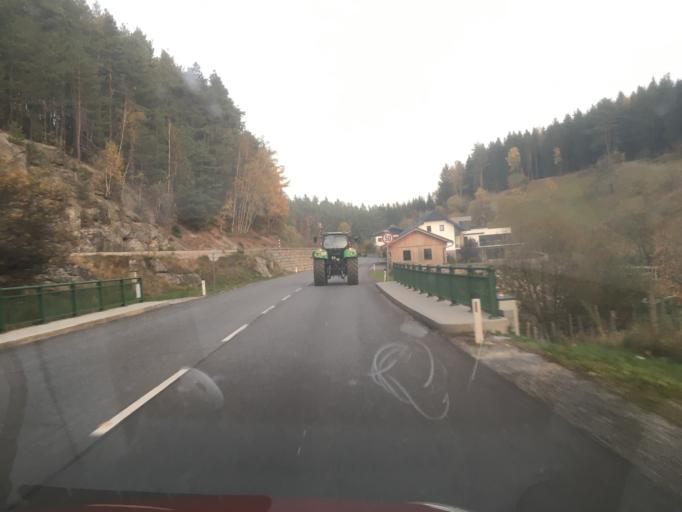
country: AT
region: Lower Austria
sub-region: Politischer Bezirk Zwettl
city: Langschlag
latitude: 48.5754
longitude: 14.8936
